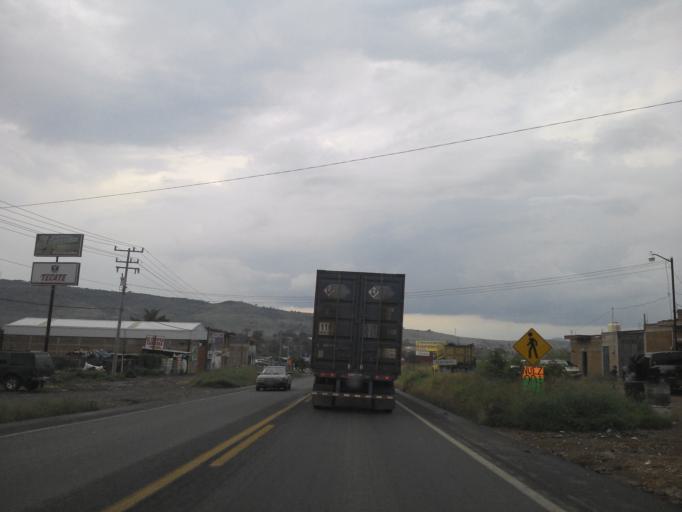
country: MX
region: Jalisco
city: Zapotlanejo
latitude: 20.6361
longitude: -103.0510
